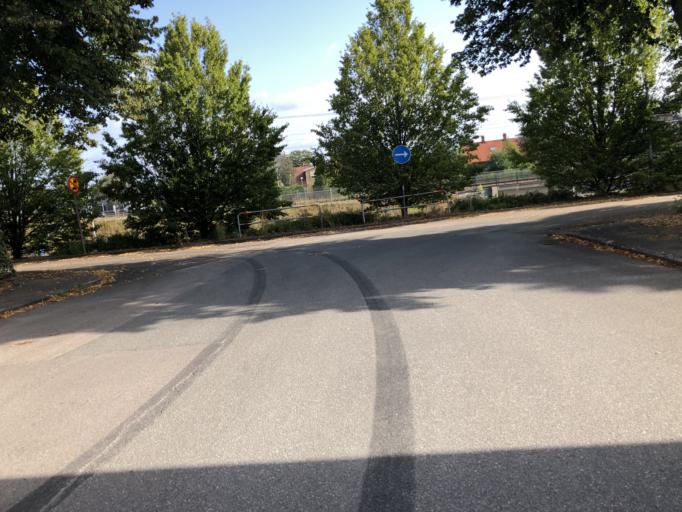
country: SE
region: Skane
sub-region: Hassleholms Kommun
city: Vinslov
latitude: 56.1041
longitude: 13.9179
